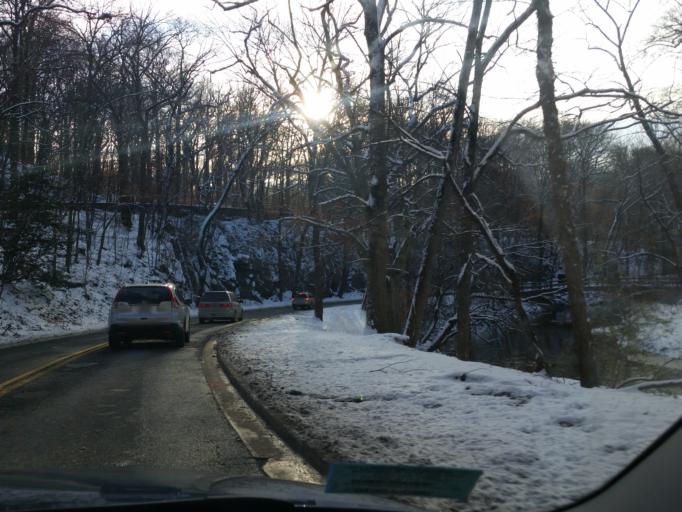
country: US
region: Maryland
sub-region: Montgomery County
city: Chevy Chase
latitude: 38.9375
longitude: -77.0484
